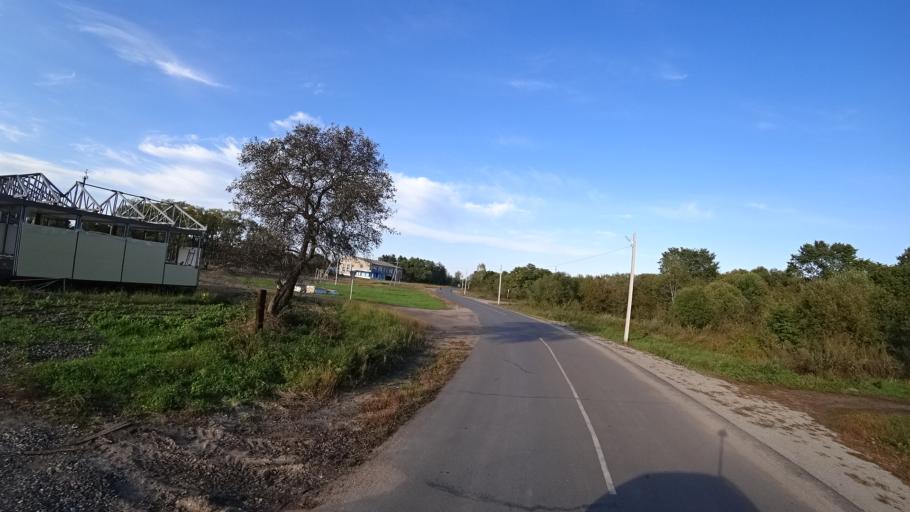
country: RU
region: Amur
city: Arkhara
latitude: 49.3620
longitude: 130.1216
